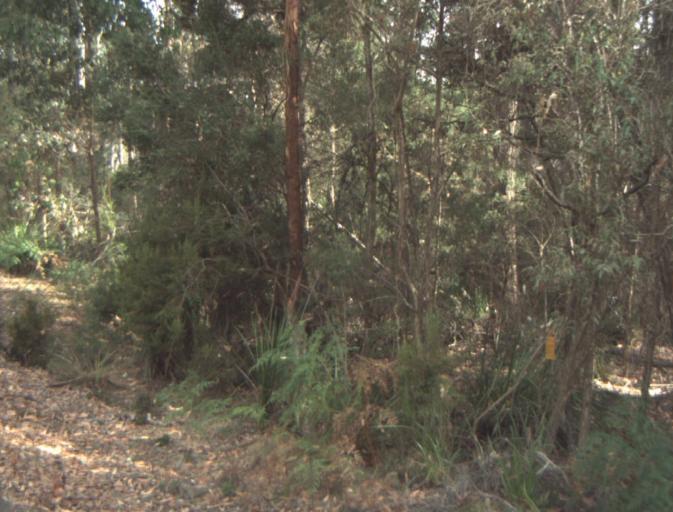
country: AU
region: Tasmania
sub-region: Launceston
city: Mayfield
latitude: -41.2639
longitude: 147.2310
